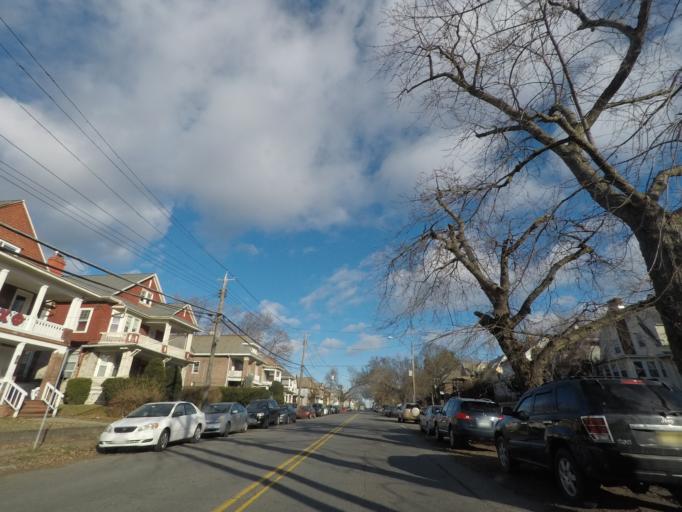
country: US
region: New York
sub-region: Rensselaer County
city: Troy
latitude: 42.7311
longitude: -73.6772
